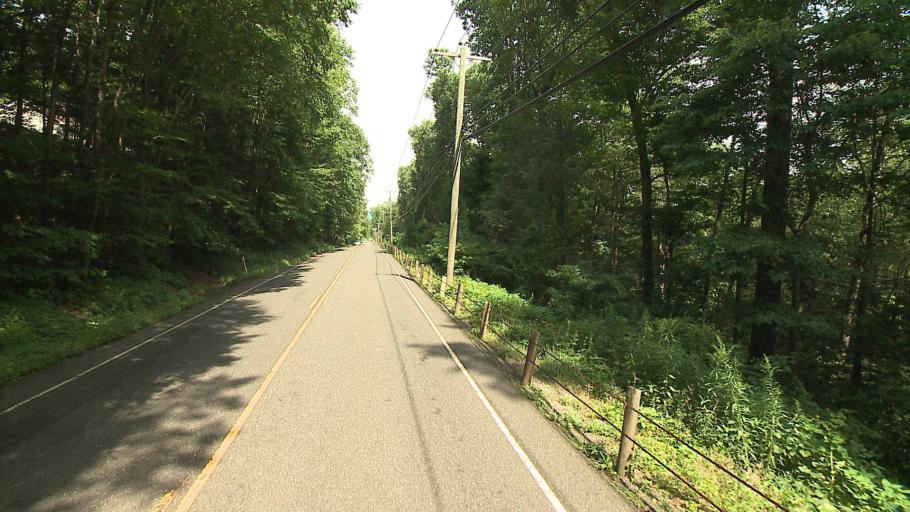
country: US
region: Connecticut
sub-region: Fairfield County
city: Sherman
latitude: 41.5638
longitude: -73.4938
